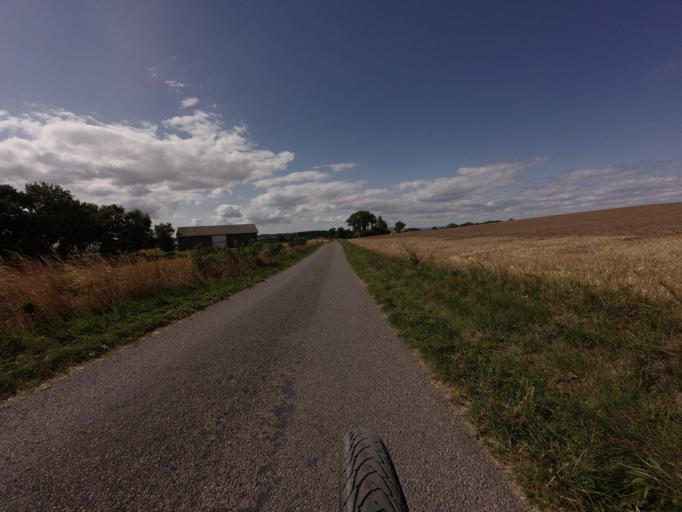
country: DK
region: Zealand
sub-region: Vordingborg Kommune
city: Stege
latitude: 55.0198
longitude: 12.4576
